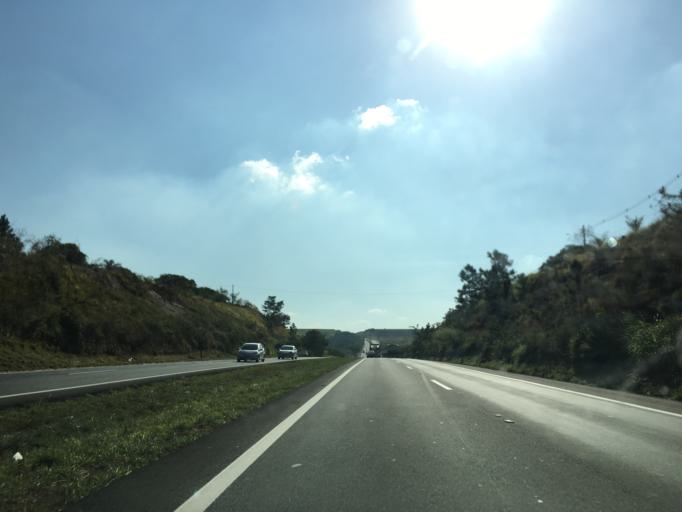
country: BR
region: Sao Paulo
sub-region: Piracicaba
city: Piracicaba
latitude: -22.7349
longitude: -47.5345
